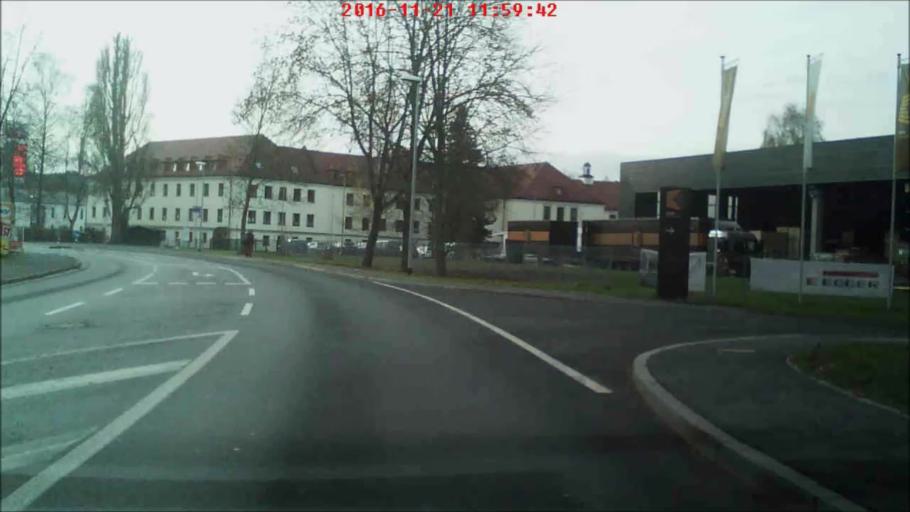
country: DE
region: Thuringia
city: Schleusingen
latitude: 50.5062
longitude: 10.7434
